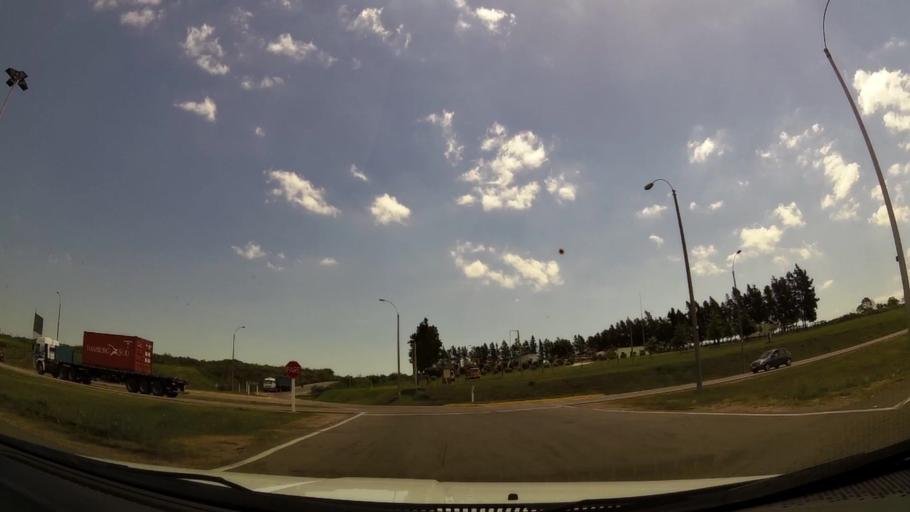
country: UY
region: Canelones
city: La Paz
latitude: -34.8152
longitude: -56.2584
